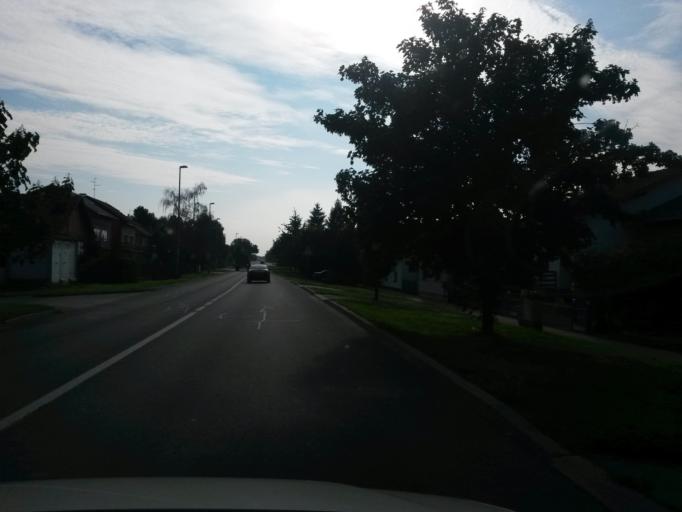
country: HR
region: Vukovarsko-Srijemska
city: Vukovar
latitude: 45.3368
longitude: 19.0253
